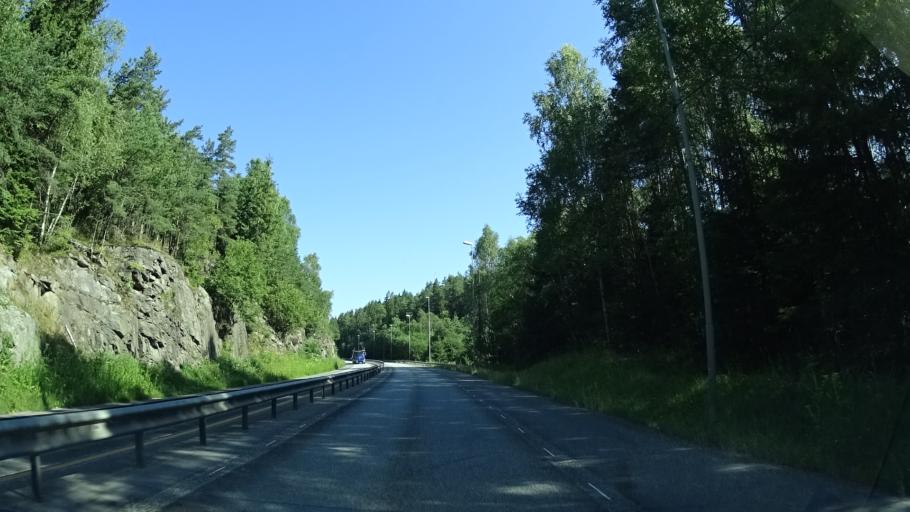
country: NO
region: Akershus
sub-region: Oppegard
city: Kolbotn
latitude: 59.7632
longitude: 10.7755
